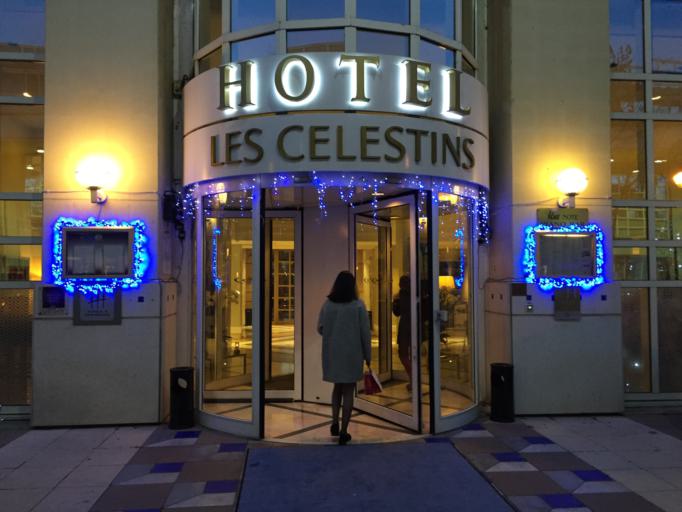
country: FR
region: Auvergne
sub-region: Departement de l'Allier
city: Vichy
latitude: 46.1258
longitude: 3.4175
